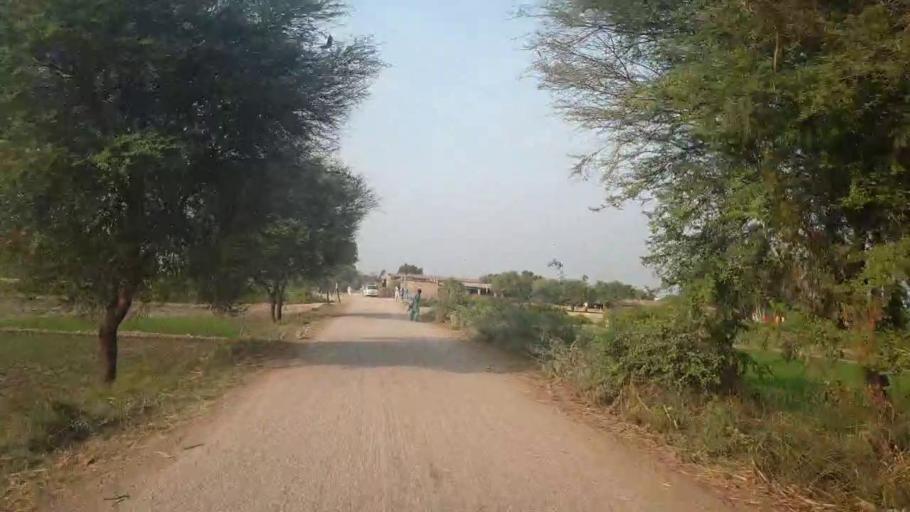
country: PK
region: Sindh
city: Tando Jam
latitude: 25.4392
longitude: 68.5620
